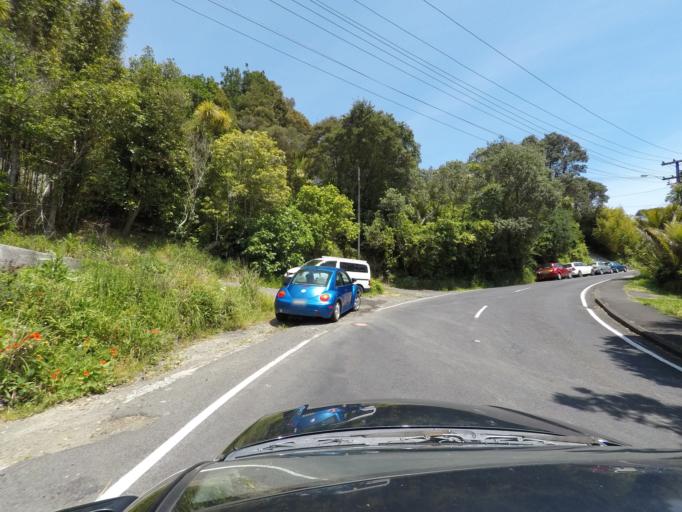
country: NZ
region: Auckland
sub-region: Auckland
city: Titirangi
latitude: -36.9688
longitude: 174.6401
